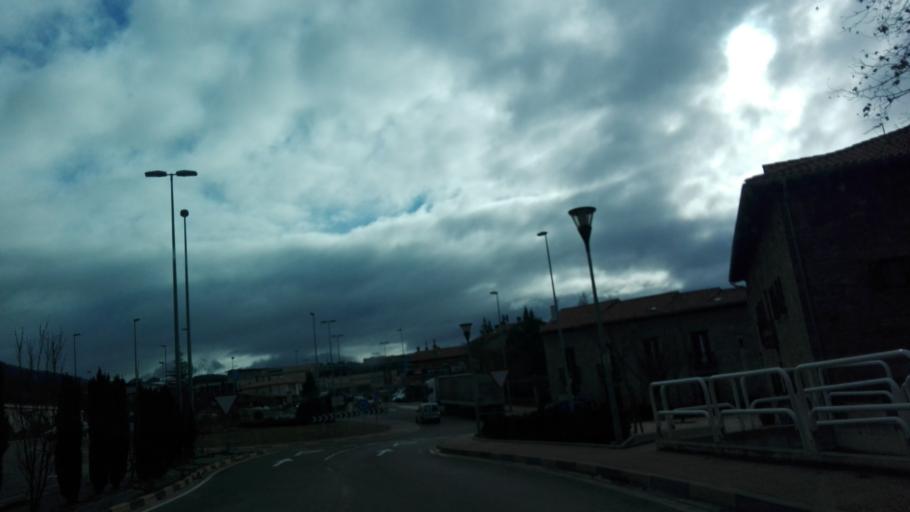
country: ES
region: Navarre
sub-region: Provincia de Navarra
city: Egues-Uharte
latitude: 42.8329
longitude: -1.5862
